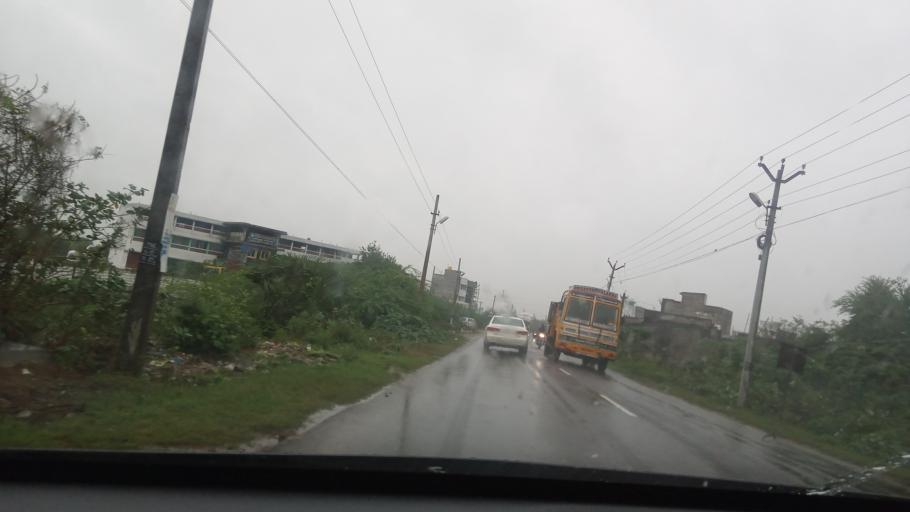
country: IN
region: Tamil Nadu
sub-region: Tiruvannamalai
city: Cheyyar
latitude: 12.6537
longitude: 79.5382
